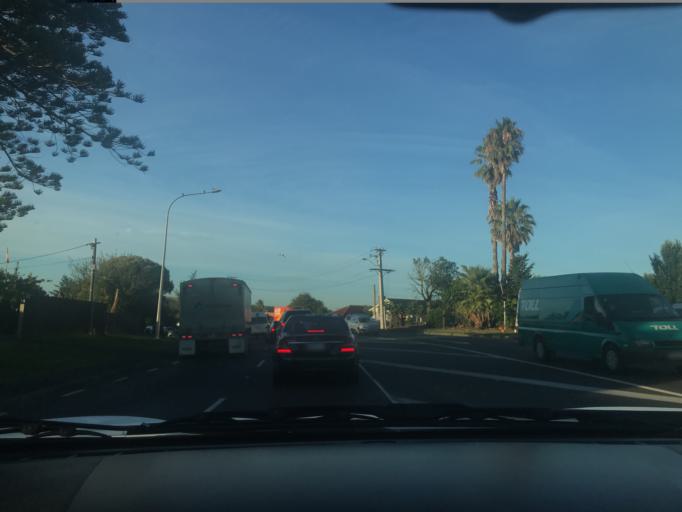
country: NZ
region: Auckland
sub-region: Auckland
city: Tamaki
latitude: -36.9098
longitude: 174.8380
